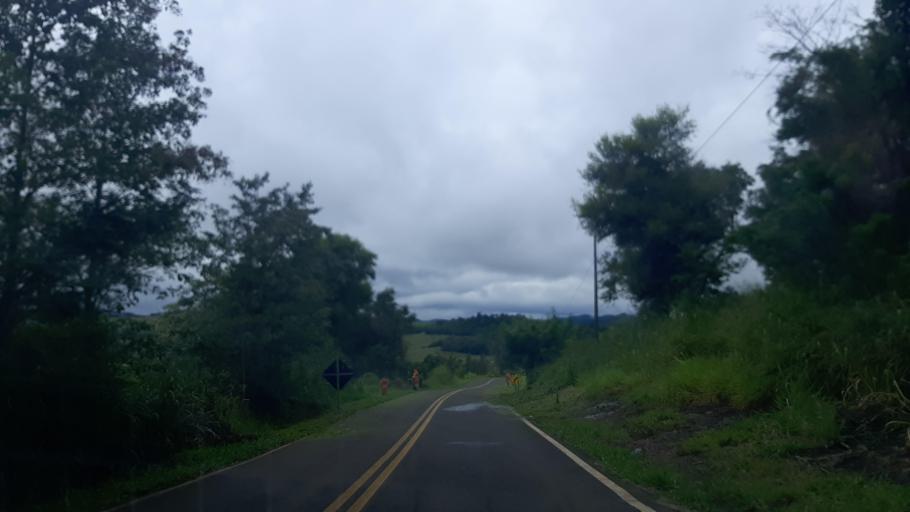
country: BR
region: Parana
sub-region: Ampere
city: Ampere
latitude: -25.9691
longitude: -53.4435
